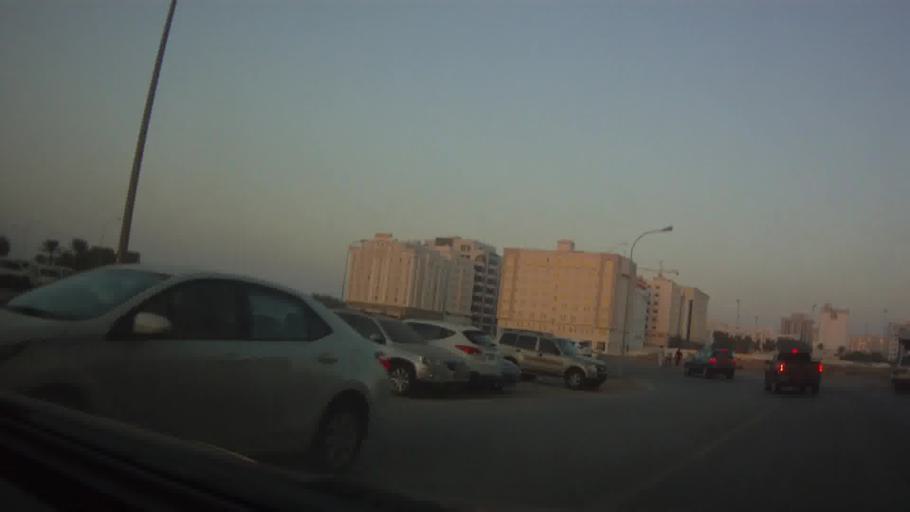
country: OM
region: Muhafazat Masqat
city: Bawshar
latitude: 23.5947
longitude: 58.4137
